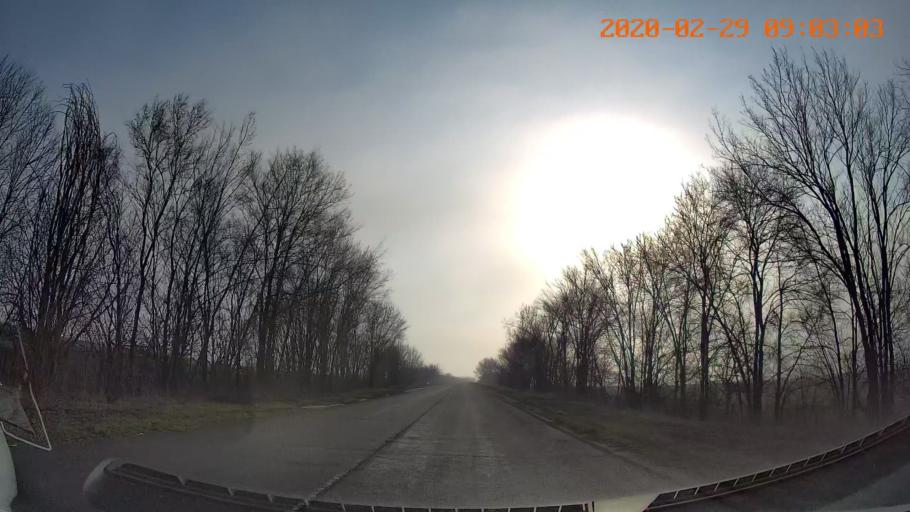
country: UA
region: Odessa
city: Velykoploske
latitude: 46.9180
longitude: 29.7214
